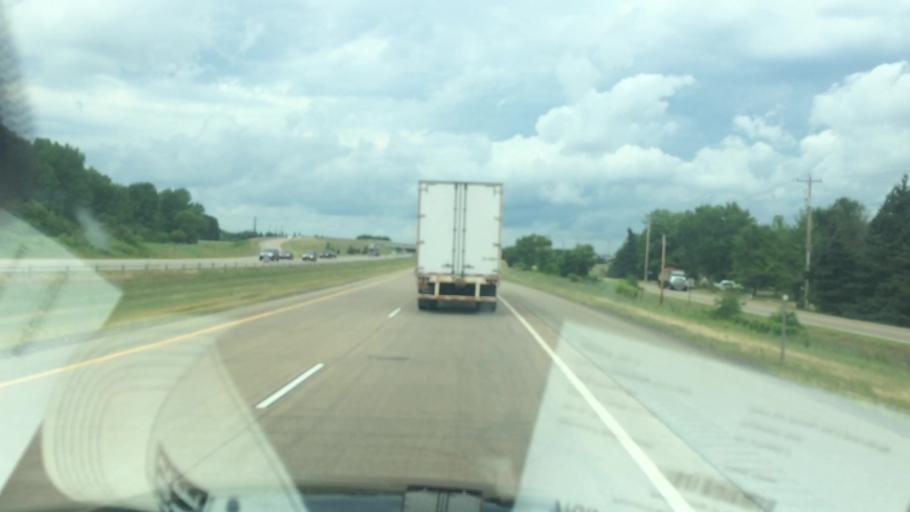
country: US
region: Wisconsin
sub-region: Marathon County
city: Rothschild
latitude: 44.8873
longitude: -89.6400
